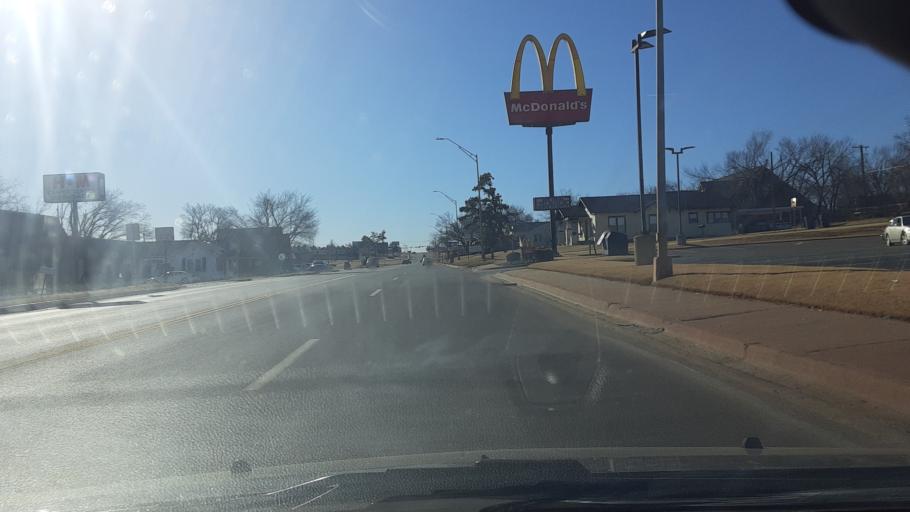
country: US
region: Oklahoma
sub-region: Logan County
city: Guthrie
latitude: 35.8612
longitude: -97.4255
